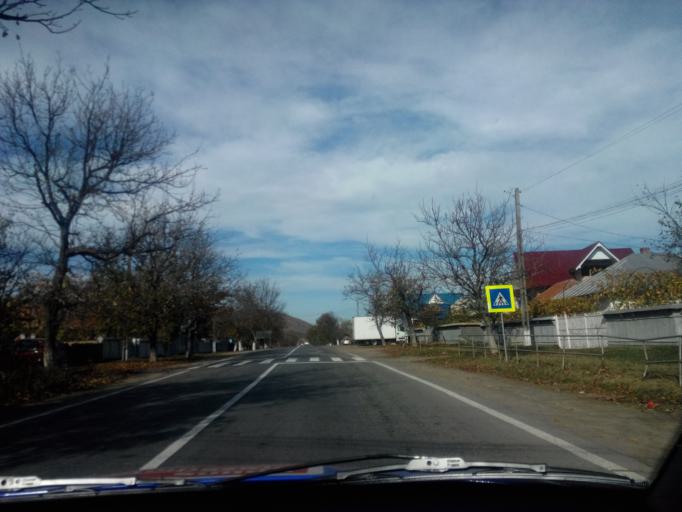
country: RO
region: Bacau
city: Gura Vaii
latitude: 46.3154
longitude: 26.7507
